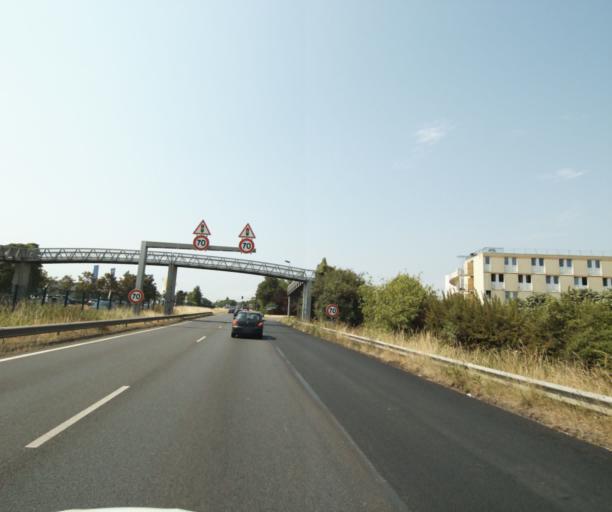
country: FR
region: Ile-de-France
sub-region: Departement des Yvelines
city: Conflans-Sainte-Honorine
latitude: 49.0038
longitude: 2.0825
